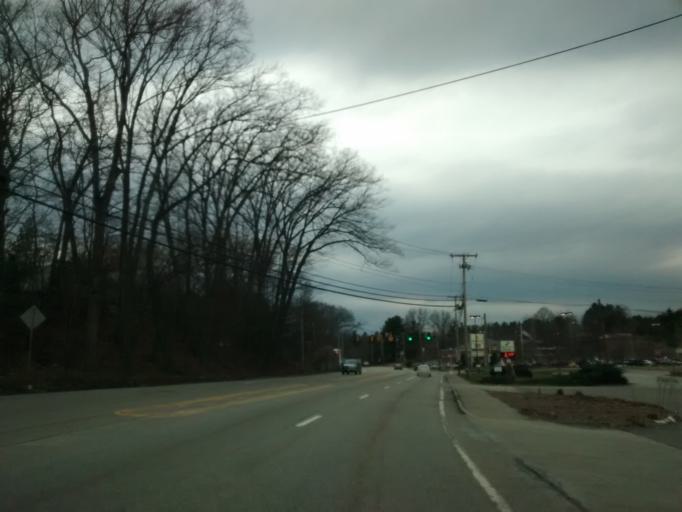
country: US
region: Massachusetts
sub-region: Worcester County
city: Grafton
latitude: 42.2183
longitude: -71.6970
